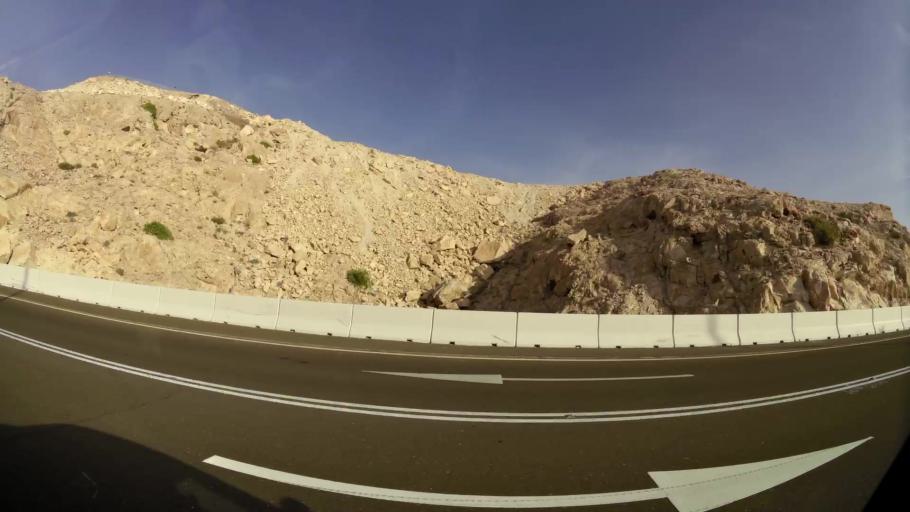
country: AE
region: Abu Dhabi
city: Al Ain
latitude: 24.0840
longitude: 55.7626
